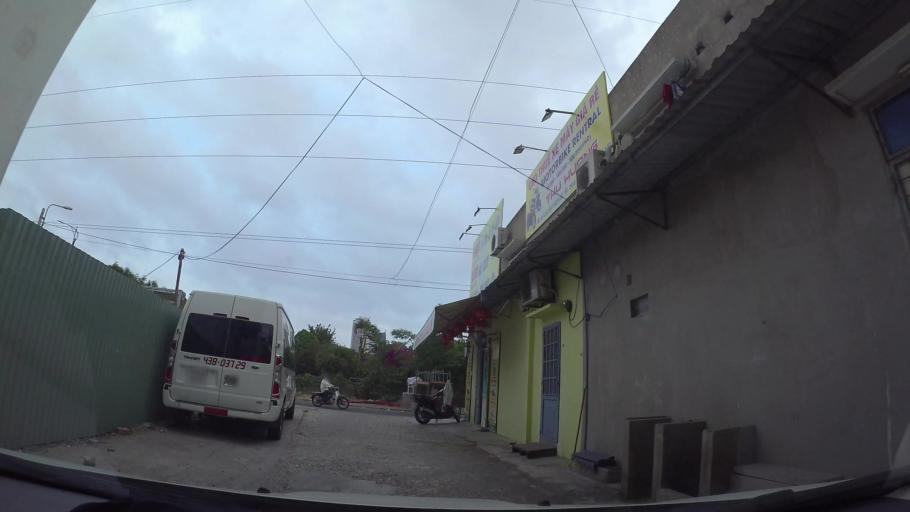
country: VN
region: Da Nang
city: Son Tra
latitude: 16.0617
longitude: 108.2383
